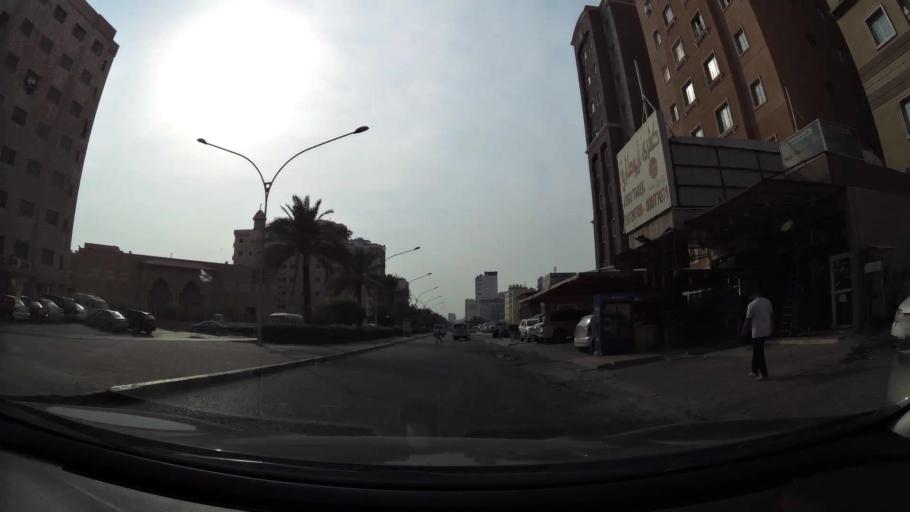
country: KW
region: Al Farwaniyah
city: Janub as Surrah
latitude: 29.2831
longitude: 47.9759
